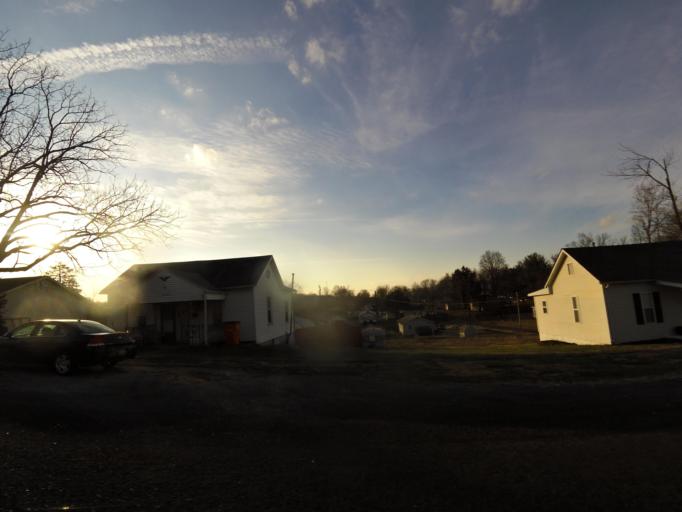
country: US
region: Illinois
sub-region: Fayette County
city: Vandalia
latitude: 38.9597
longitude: -89.1057
